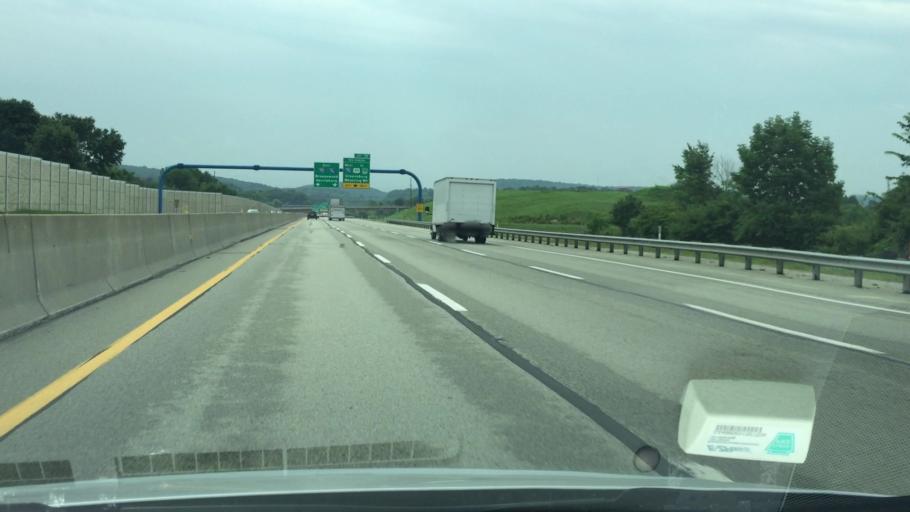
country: US
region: Pennsylvania
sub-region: Westmoreland County
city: New Stanton
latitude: 40.2300
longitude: -79.6154
